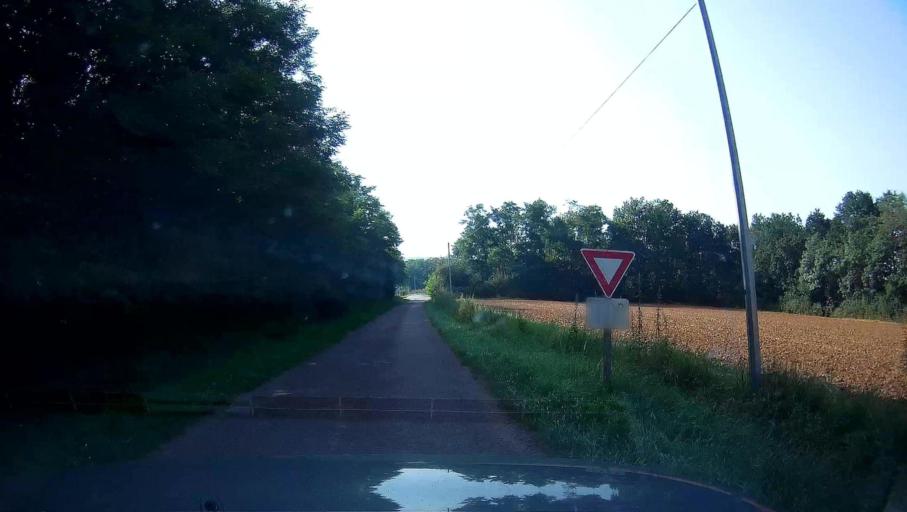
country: FR
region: Bourgogne
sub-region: Departement de Saone-et-Loire
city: Saint-Leger-sur-Dheune
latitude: 46.8745
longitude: 4.6317
